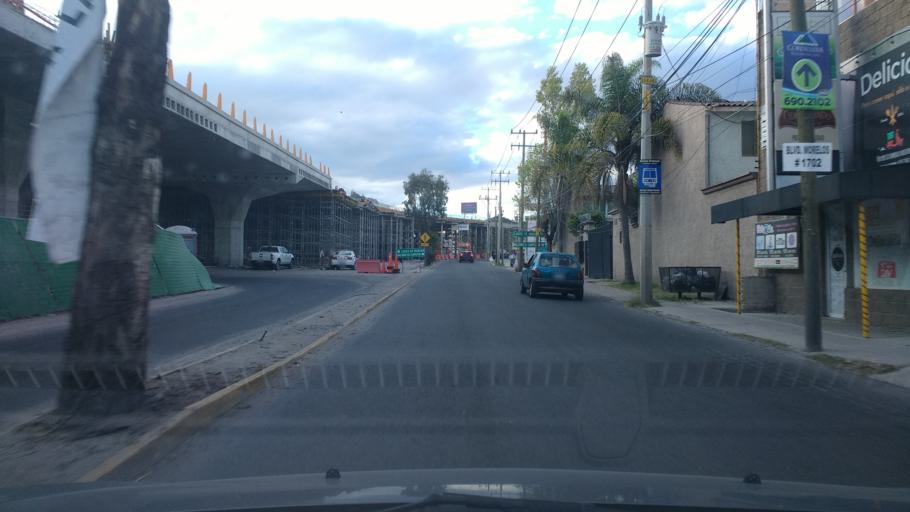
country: MX
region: Guanajuato
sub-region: Leon
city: La Ermita
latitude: 21.1698
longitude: -101.6969
